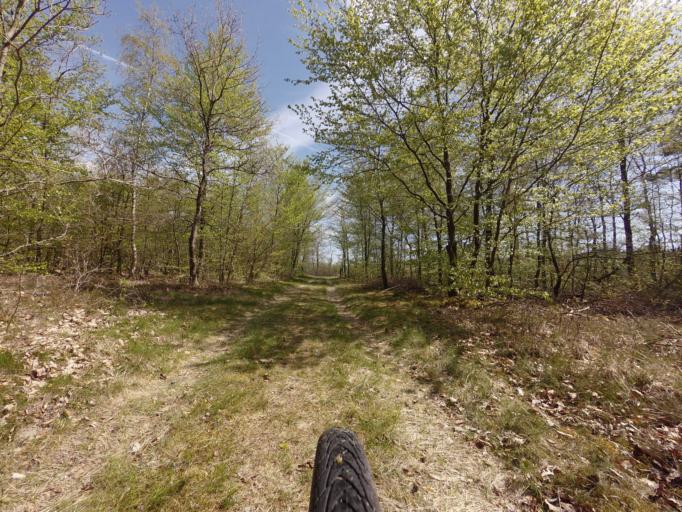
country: DK
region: North Denmark
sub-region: Jammerbugt Kommune
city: Brovst
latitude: 57.1635
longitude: 9.5743
